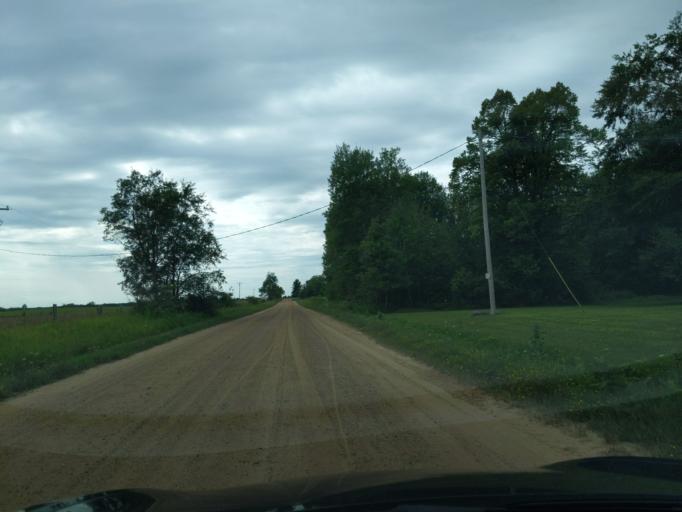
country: US
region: Michigan
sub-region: Clare County
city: Harrison
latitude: 44.0025
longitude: -84.9845
